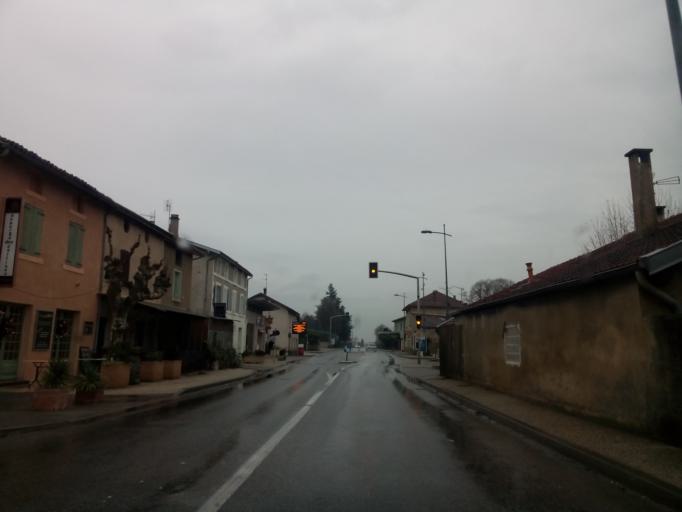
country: FR
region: Rhone-Alpes
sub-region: Departement de la Drome
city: Clerieux
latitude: 45.0507
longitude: 4.9824
